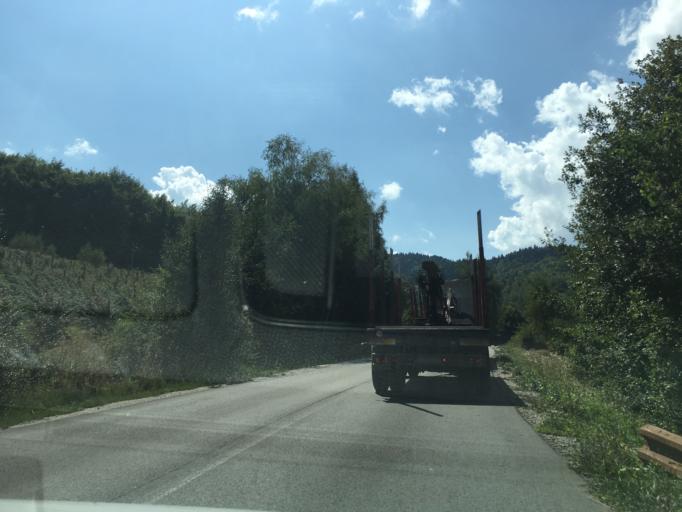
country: RS
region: Central Serbia
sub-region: Zlatiborski Okrug
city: Prijepolje
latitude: 43.3314
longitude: 19.5473
